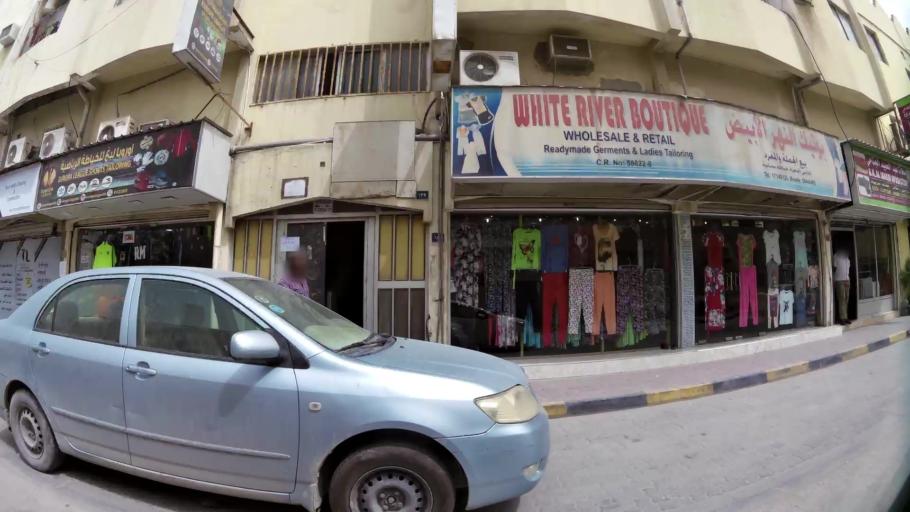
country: BH
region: Northern
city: Madinat `Isa
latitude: 26.1855
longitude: 50.5425
